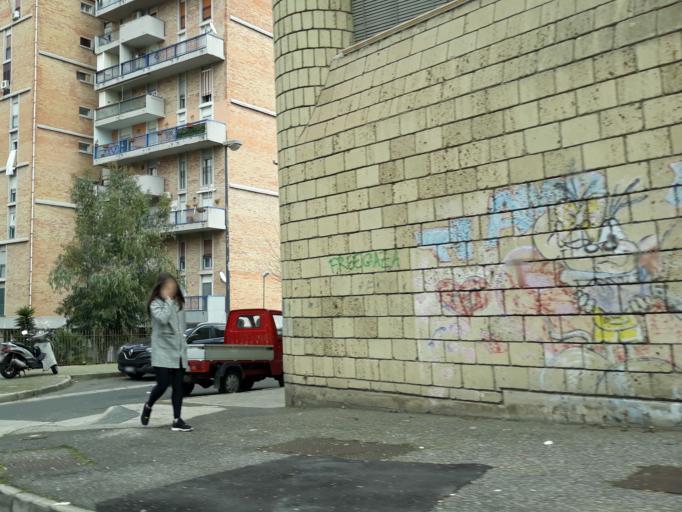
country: IT
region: Campania
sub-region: Provincia di Napoli
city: Melito di Napoli
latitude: 40.8914
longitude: 14.2341
